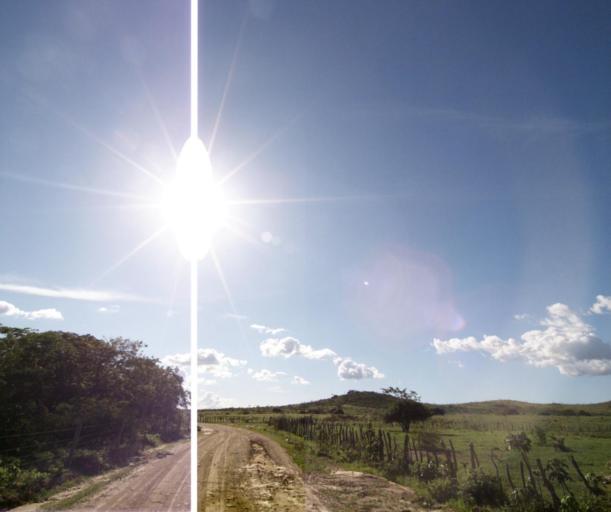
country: BR
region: Bahia
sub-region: Tanhacu
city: Tanhacu
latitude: -14.1883
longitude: -40.9644
